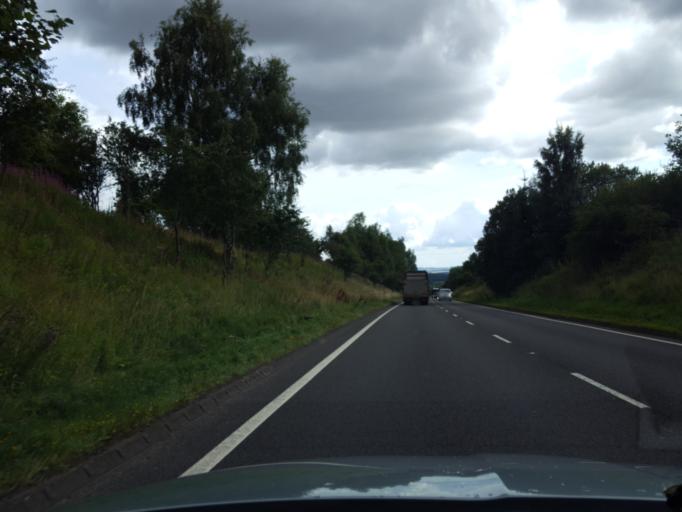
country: GB
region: Scotland
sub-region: Perth and Kinross
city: Bankfoot
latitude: 56.5056
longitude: -3.5109
